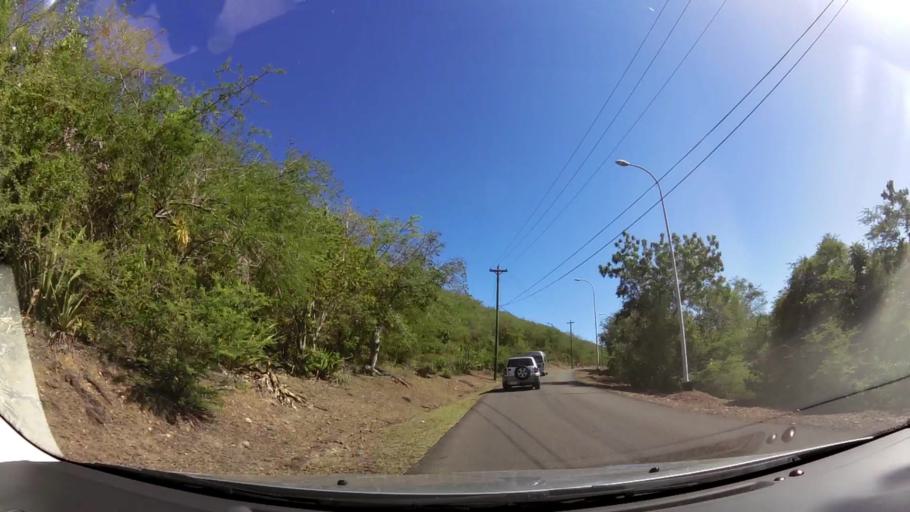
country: AG
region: Saint Paul
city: Falmouth
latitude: 17.0109
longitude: -61.7602
